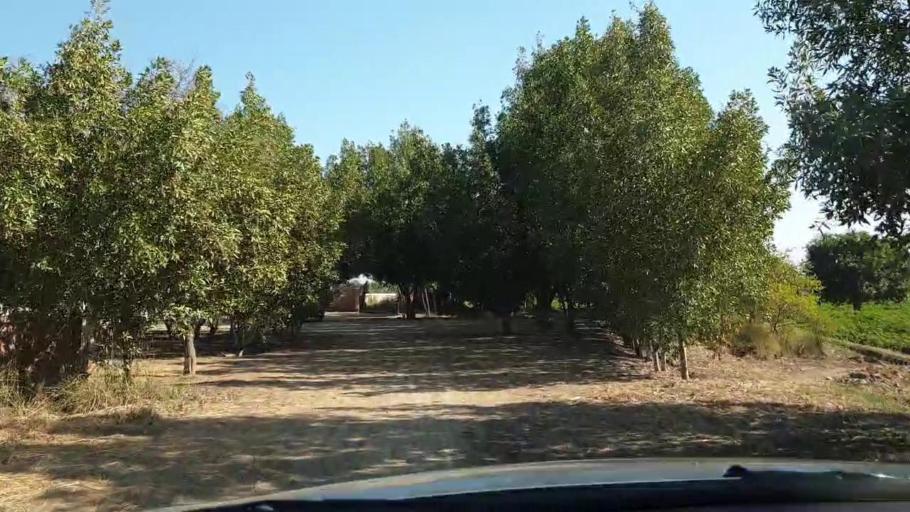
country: PK
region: Sindh
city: Jhol
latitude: 25.9338
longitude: 68.9491
